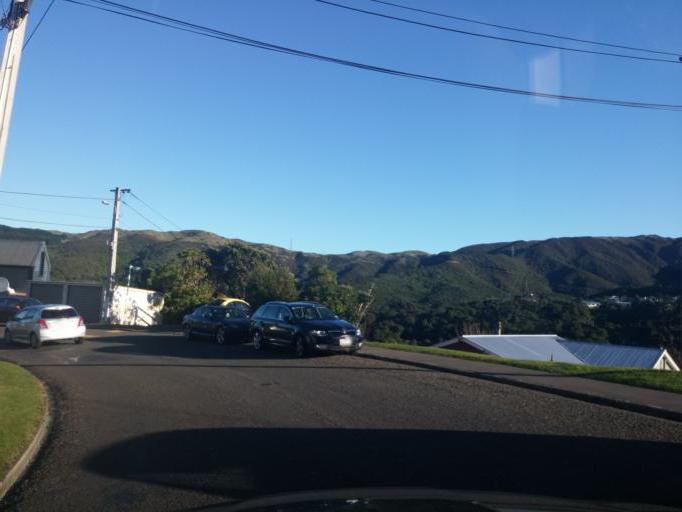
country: NZ
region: Wellington
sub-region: Wellington City
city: Kelburn
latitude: -41.2663
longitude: 174.7647
